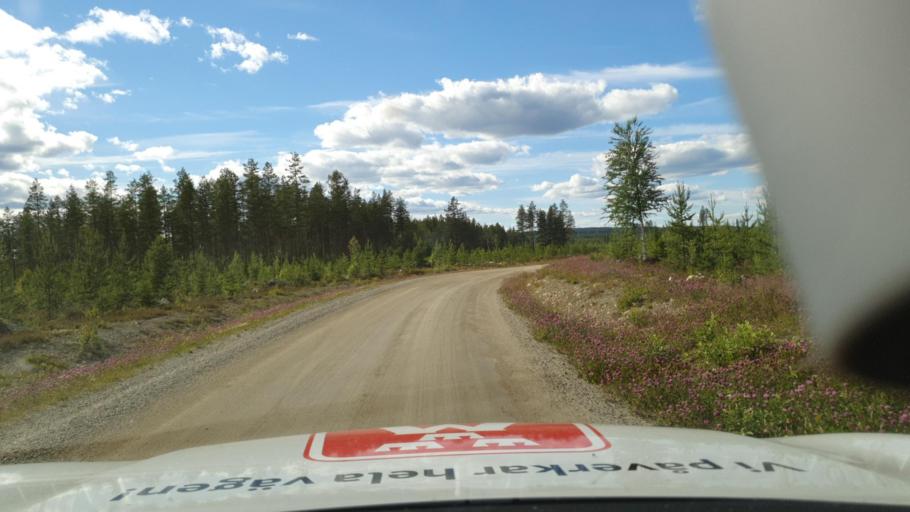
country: SE
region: Vaesterbotten
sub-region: Lycksele Kommun
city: Lycksele
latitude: 64.3941
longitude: 18.5873
